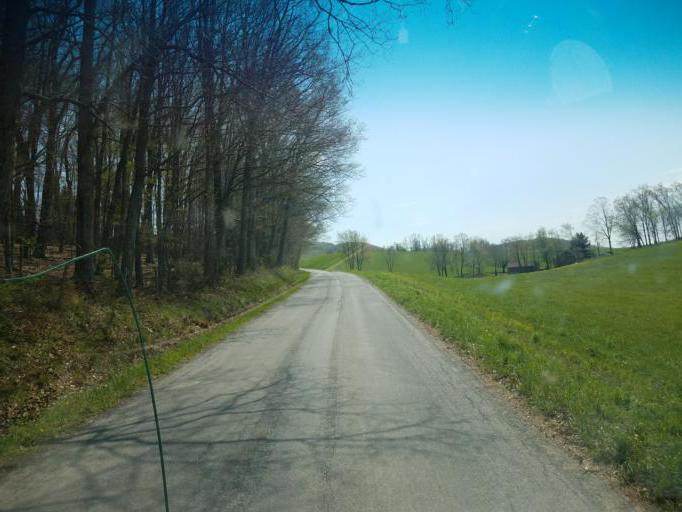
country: US
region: Virginia
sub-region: Smyth County
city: Marion
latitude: 36.7661
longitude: -81.4569
